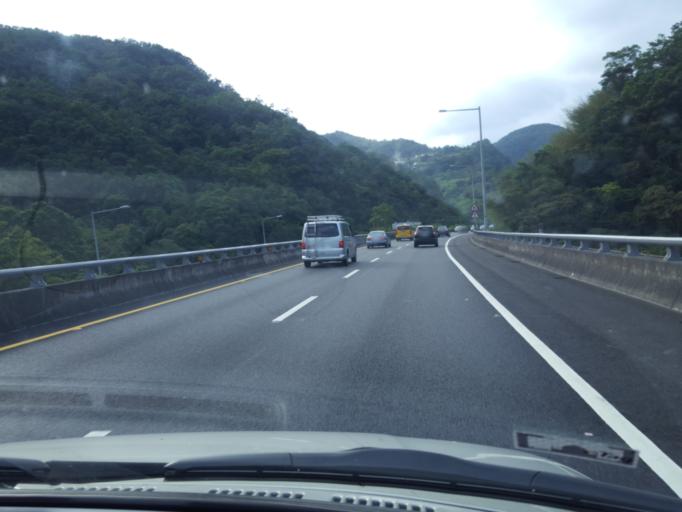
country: TW
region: Taiwan
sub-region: Keelung
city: Keelung
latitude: 24.9467
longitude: 121.7073
